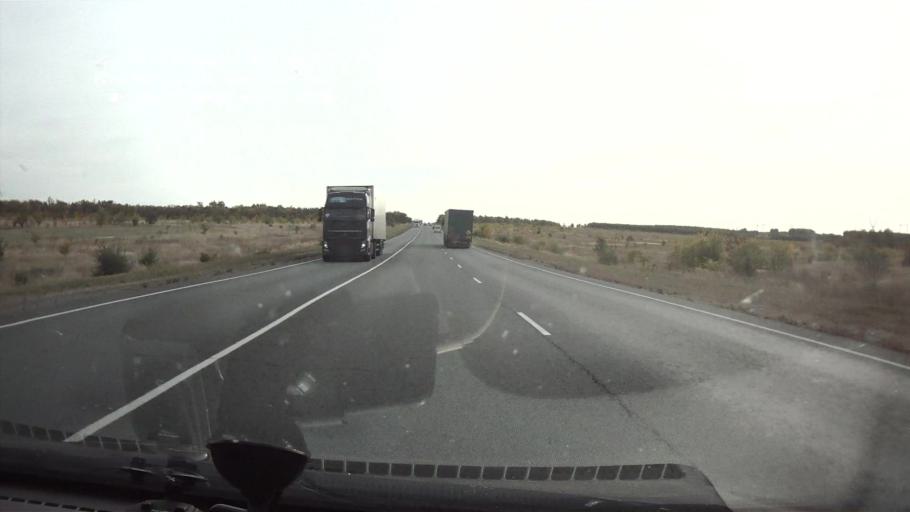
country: RU
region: Saratov
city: Sinodskoye
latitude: 51.9165
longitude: 46.5575
